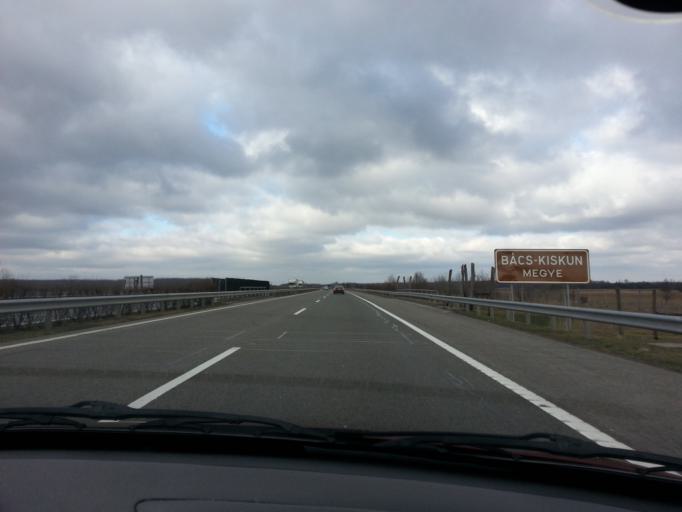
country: HU
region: Csongrad
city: Csengele
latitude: 46.5719
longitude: 19.8751
